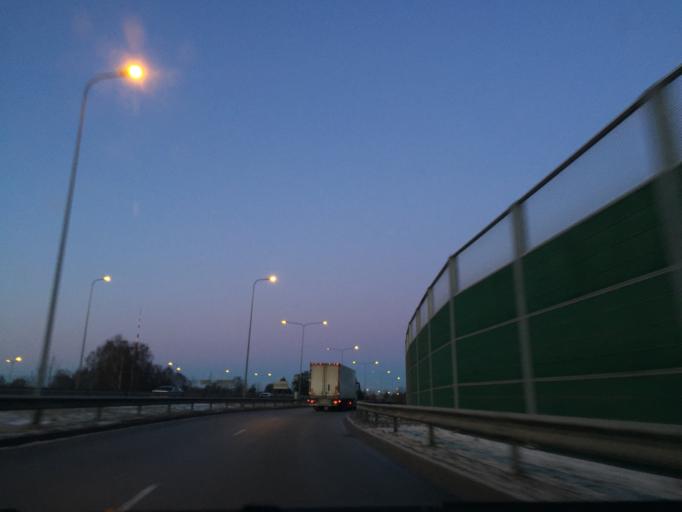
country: LV
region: Kekava
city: Balozi
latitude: 56.9026
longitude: 24.1347
